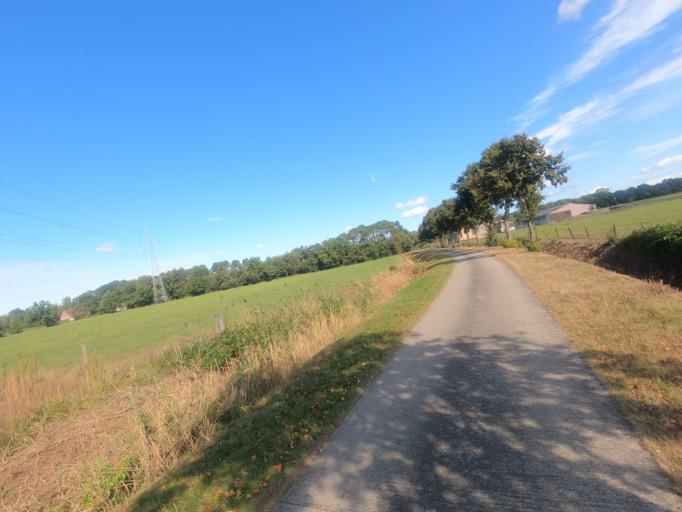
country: BE
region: Flanders
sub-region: Provincie Antwerpen
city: Lille
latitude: 51.2521
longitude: 4.8499
